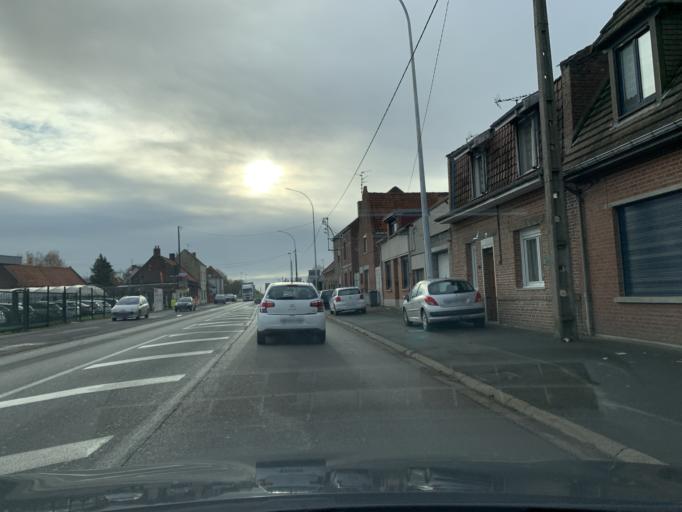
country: FR
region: Nord-Pas-de-Calais
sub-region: Departement du Nord
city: Lambres-lez-Douai
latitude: 50.3488
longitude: 3.0885
